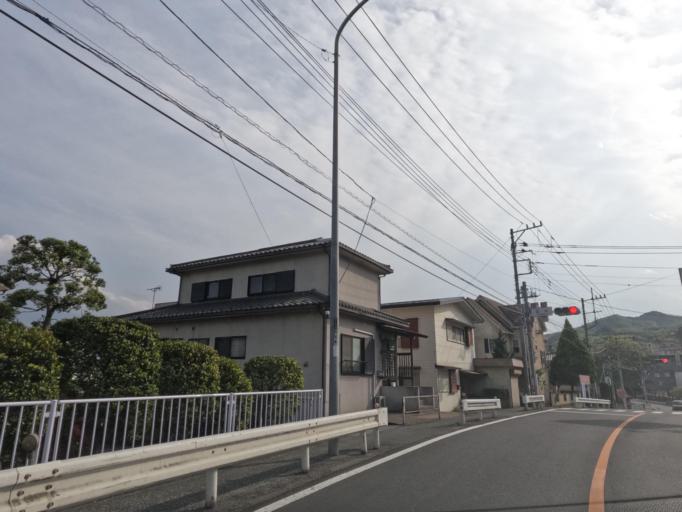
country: JP
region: Saitama
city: Chichibu
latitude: 36.0792
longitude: 139.0927
